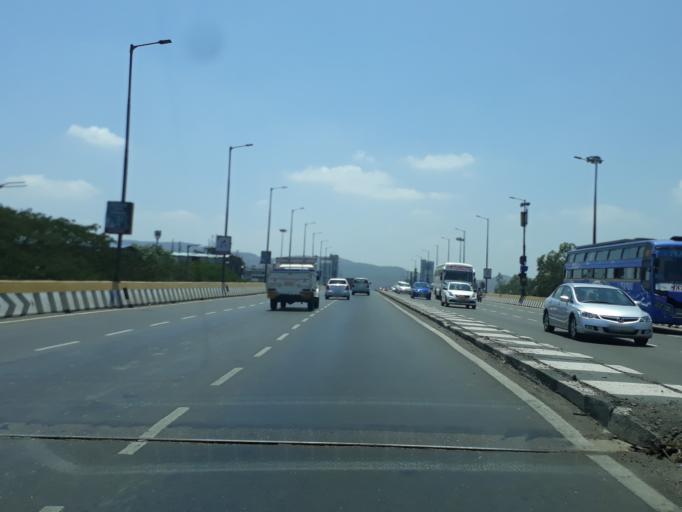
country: IN
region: Maharashtra
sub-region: Thane
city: Navi Mumbai
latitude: 19.0689
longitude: 72.9952
